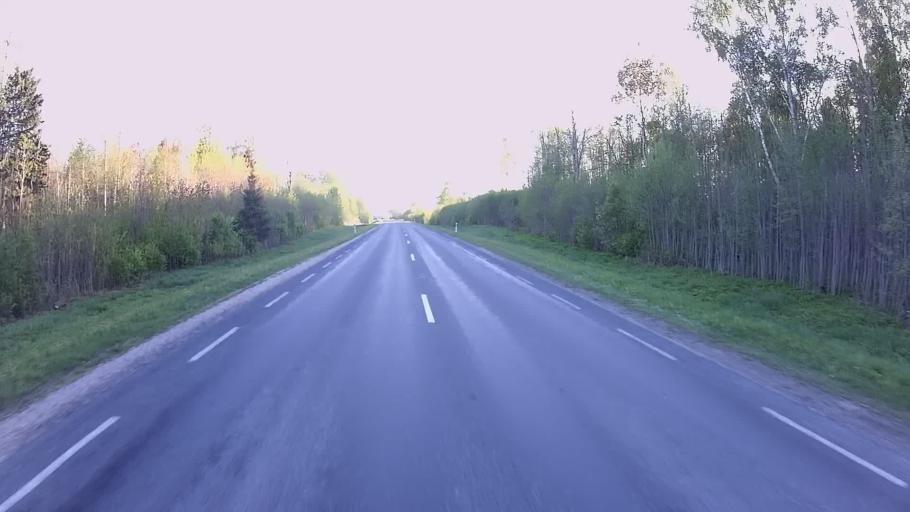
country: EE
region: Viljandimaa
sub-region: Viiratsi vald
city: Viiratsi
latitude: 58.4288
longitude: 25.7149
